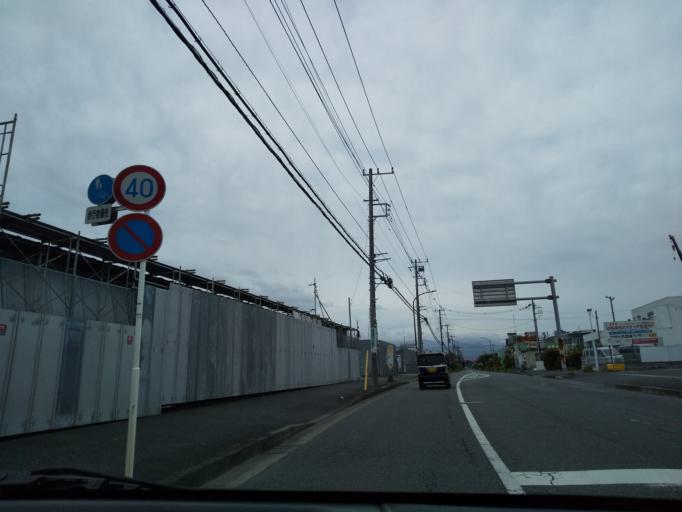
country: JP
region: Tokyo
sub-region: Machida-shi
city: Machida
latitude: 35.5328
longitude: 139.4054
